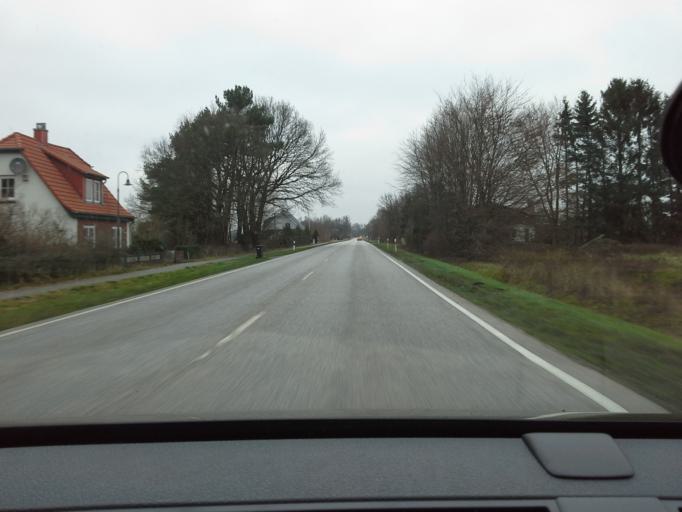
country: DE
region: Schleswig-Holstein
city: Bilsen
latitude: 53.7785
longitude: 9.8754
